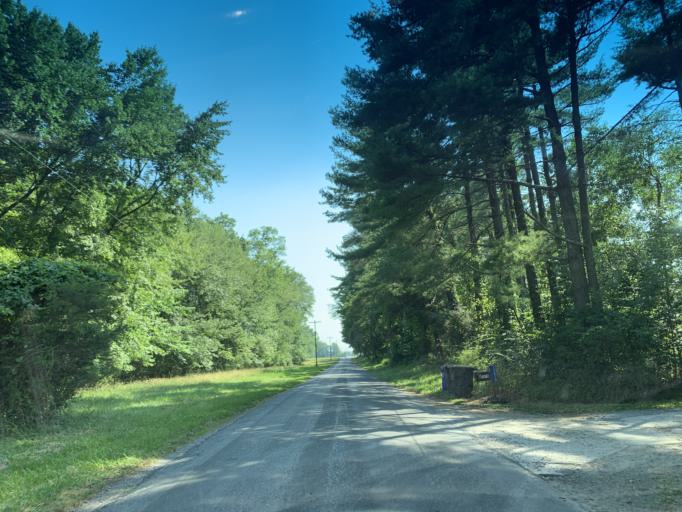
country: US
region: Maryland
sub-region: Montgomery County
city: Poolesville
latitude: 39.1136
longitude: -77.4616
